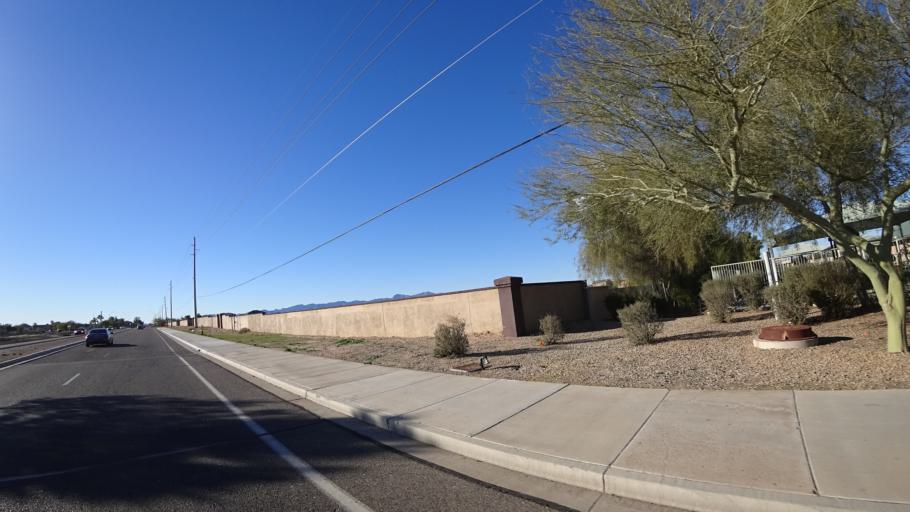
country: US
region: Arizona
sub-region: Maricopa County
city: Goodyear
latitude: 33.4500
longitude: -112.3954
